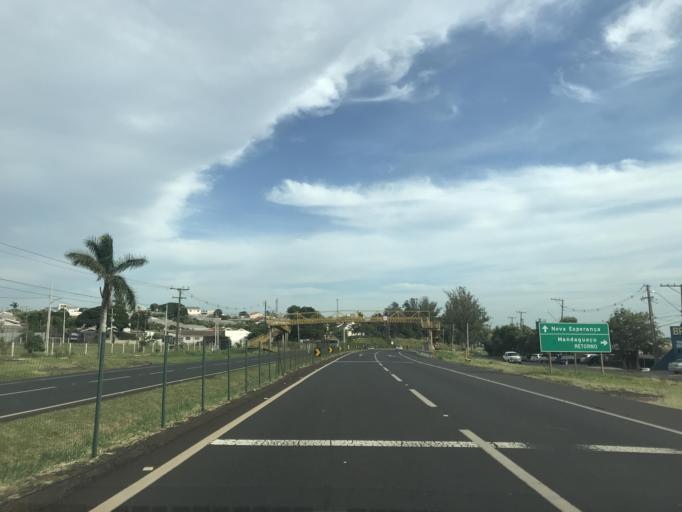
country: BR
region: Parana
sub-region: Mandaguacu
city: Mandaguacu
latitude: -23.3551
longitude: -52.0903
